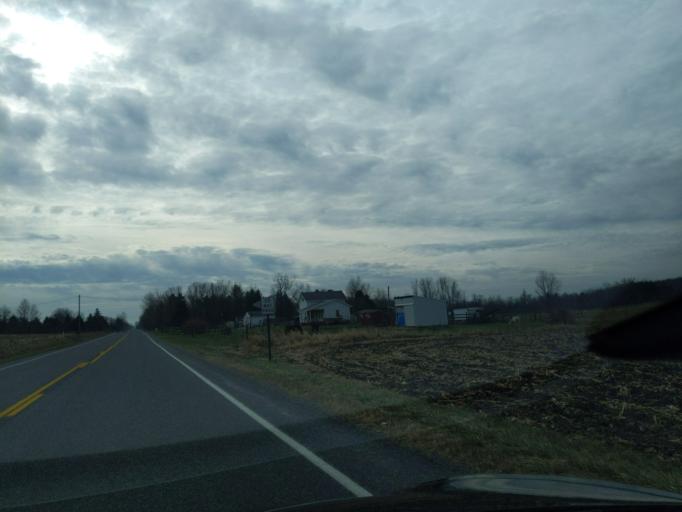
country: US
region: Michigan
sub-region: Ingham County
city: Mason
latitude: 42.5517
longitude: -84.5226
